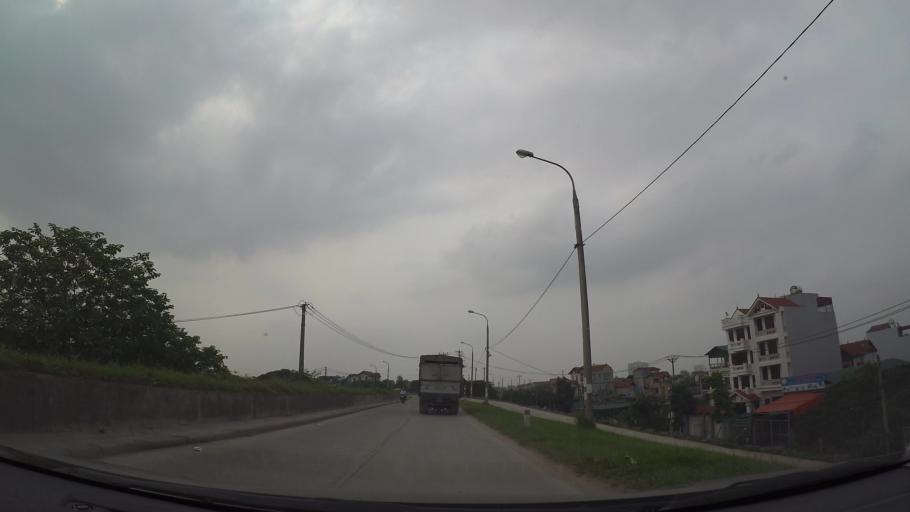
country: VN
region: Ha Noi
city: Trau Quy
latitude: 21.0041
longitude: 105.9085
